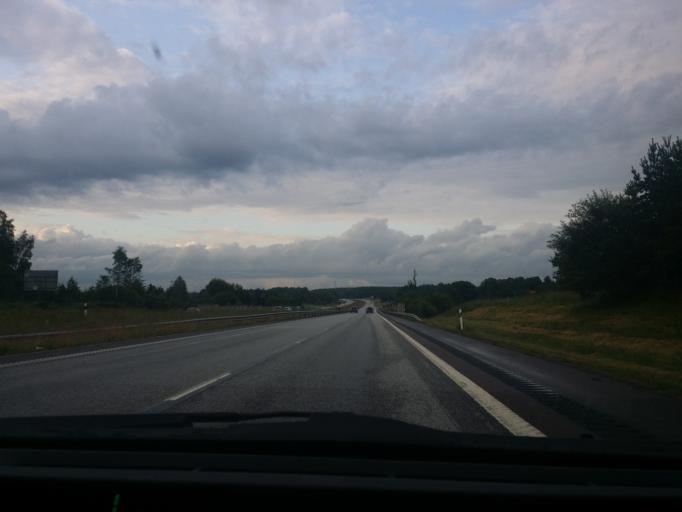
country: SE
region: Vaestmanland
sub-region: Kopings Kommun
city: Koping
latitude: 59.4951
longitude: 15.9246
